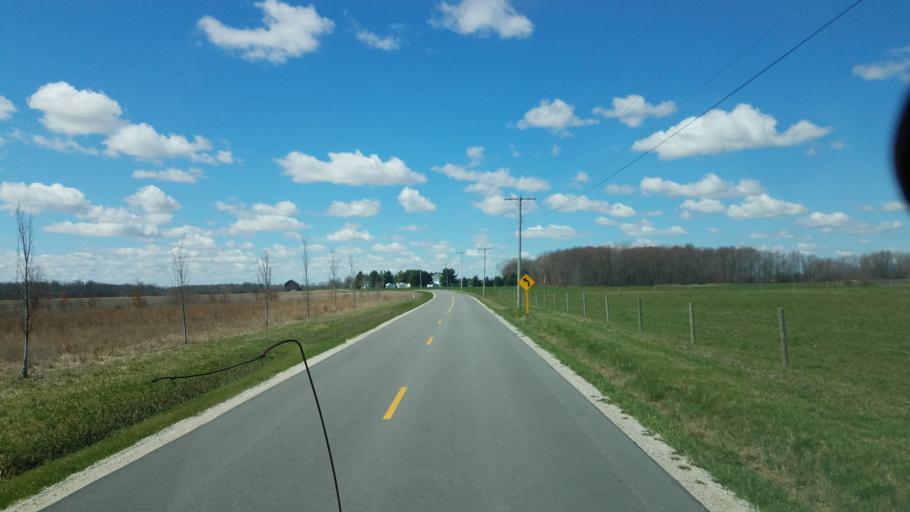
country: US
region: Ohio
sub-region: Seneca County
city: Fostoria
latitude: 41.1580
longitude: -83.4764
